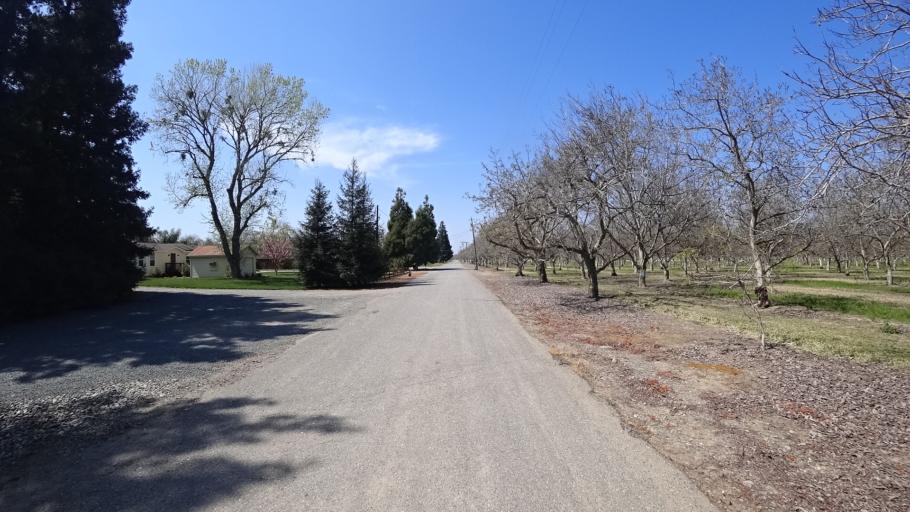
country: US
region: California
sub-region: Glenn County
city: Willows
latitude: 39.5037
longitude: -122.0107
